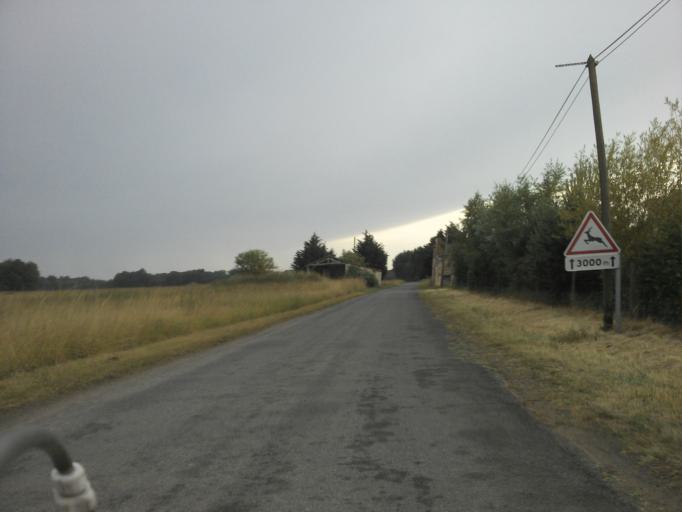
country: FR
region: Pays de la Loire
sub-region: Departement de Maine-et-Loire
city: Breze
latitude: 47.1065
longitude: -0.0049
